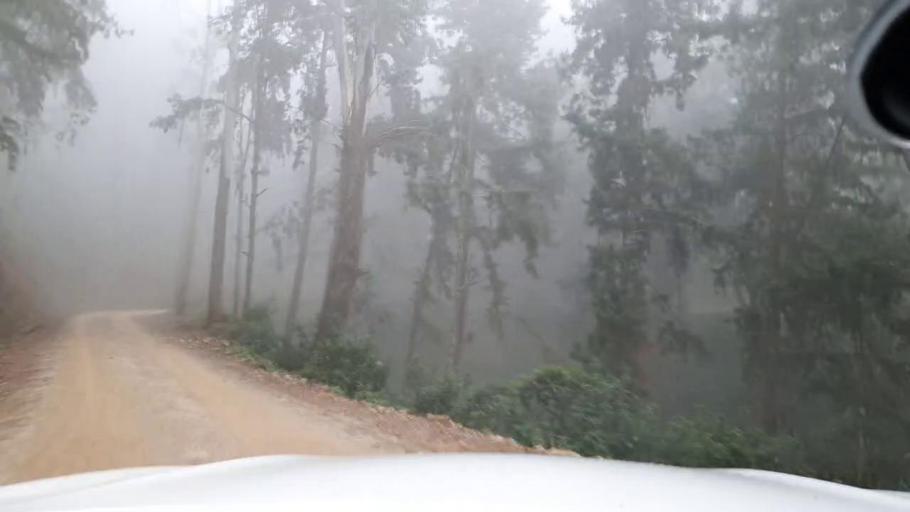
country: BI
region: Cibitoke
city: Cibitoke
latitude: -2.5934
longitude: 29.1938
